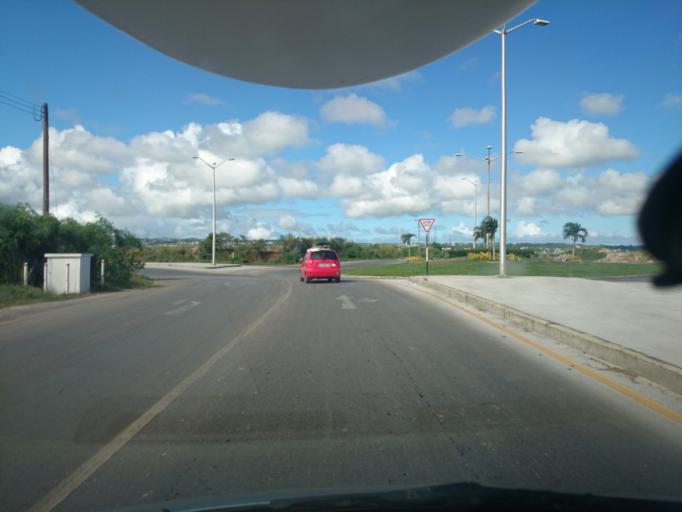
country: BB
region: Christ Church
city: Oistins
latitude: 13.0986
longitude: -59.5283
